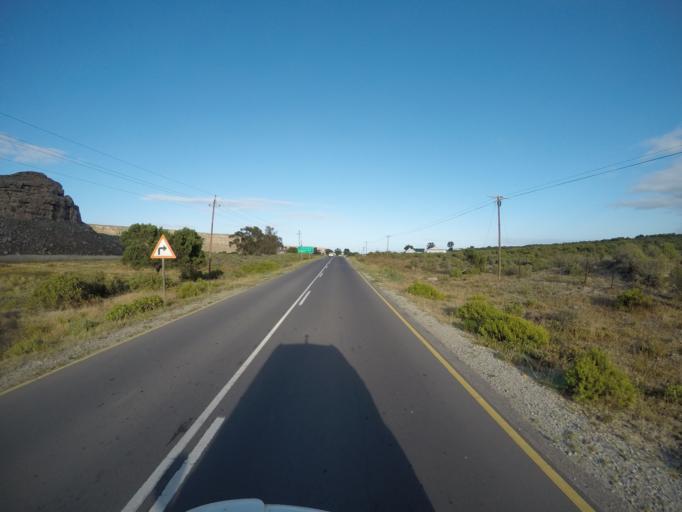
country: ZA
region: Western Cape
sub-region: West Coast District Municipality
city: Clanwilliam
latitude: -32.3131
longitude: 18.3584
